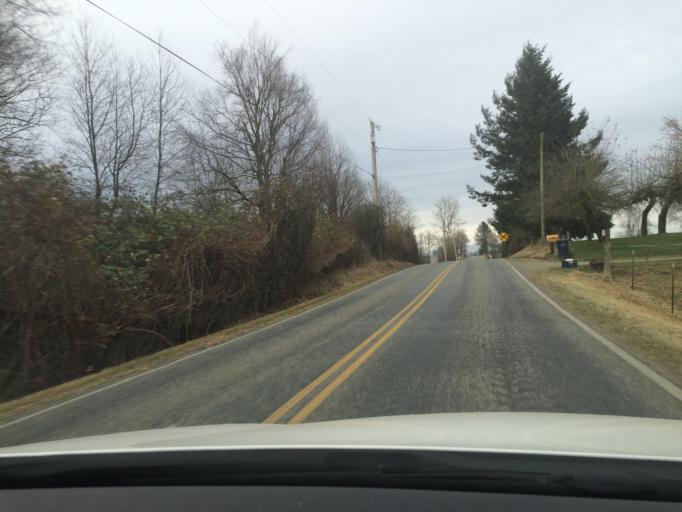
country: US
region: Washington
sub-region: Whatcom County
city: Everson
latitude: 48.9479
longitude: -122.3524
